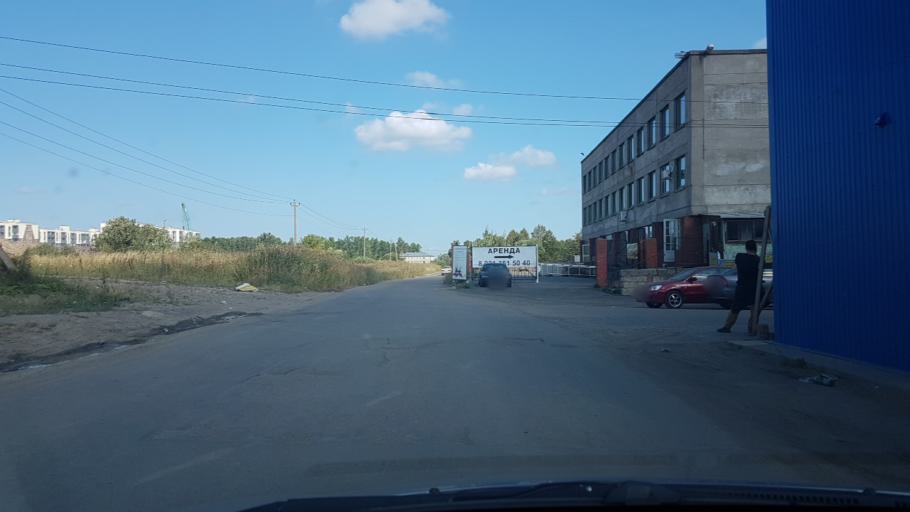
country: RU
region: St.-Petersburg
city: Sosnovaya Polyana
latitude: 59.8420
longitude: 30.1197
